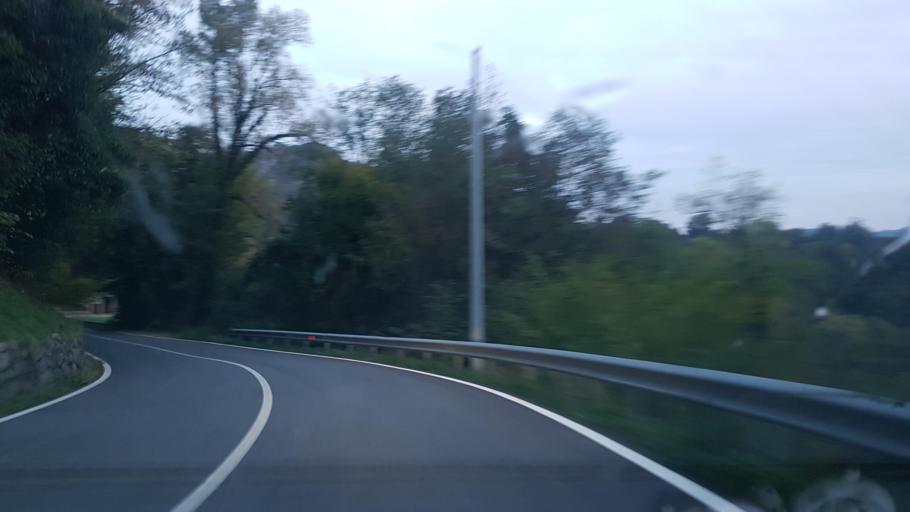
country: IT
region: Friuli Venezia Giulia
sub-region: Provincia di Pordenone
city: Anduins
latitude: 46.2302
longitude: 12.9584
